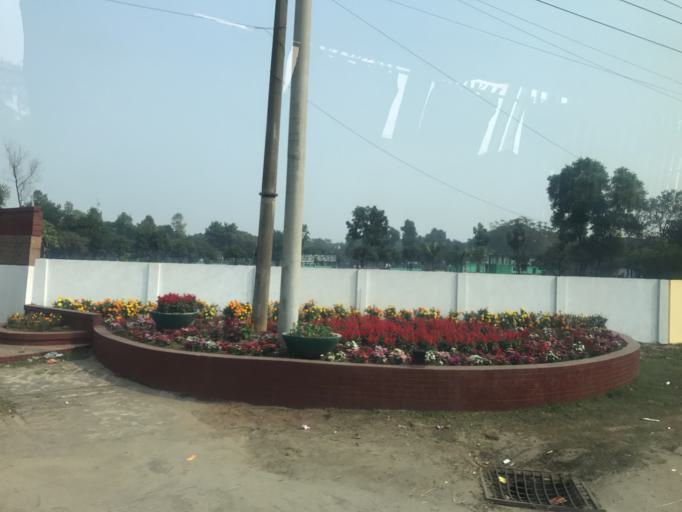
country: BD
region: Dhaka
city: Tungi
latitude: 23.9056
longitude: 90.2671
